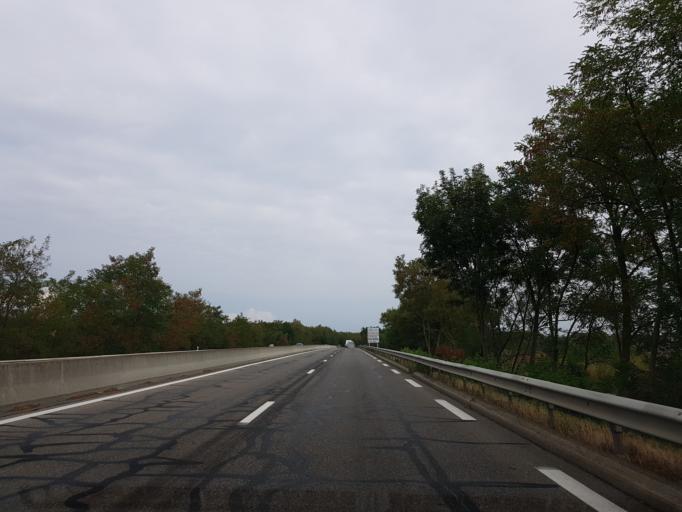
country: FR
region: Alsace
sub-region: Departement du Haut-Rhin
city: Bollwiller
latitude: 47.8418
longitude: 7.2769
